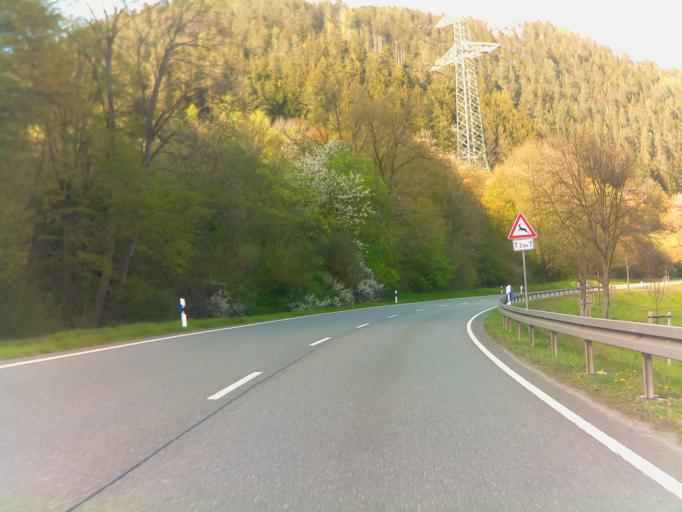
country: DE
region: Thuringia
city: Probstzella
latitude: 50.5694
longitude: 11.3573
